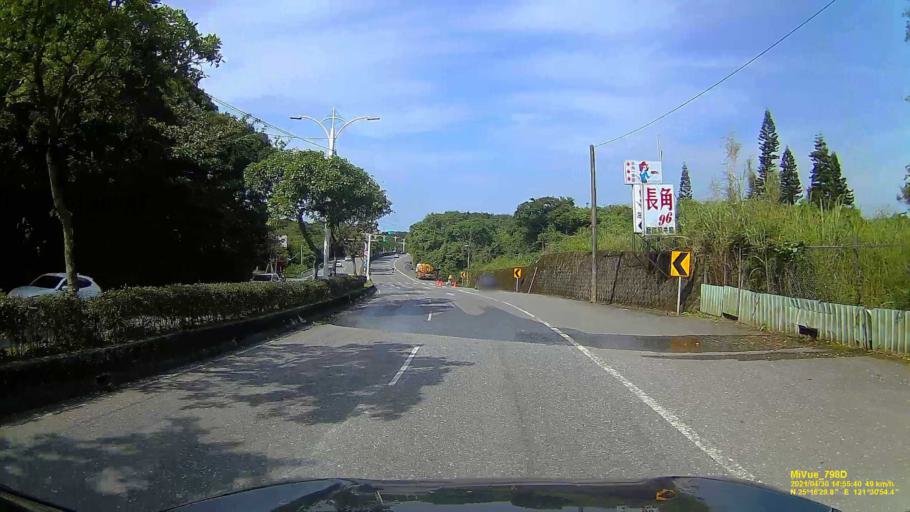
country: TW
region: Taipei
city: Taipei
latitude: 25.2751
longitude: 121.5154
